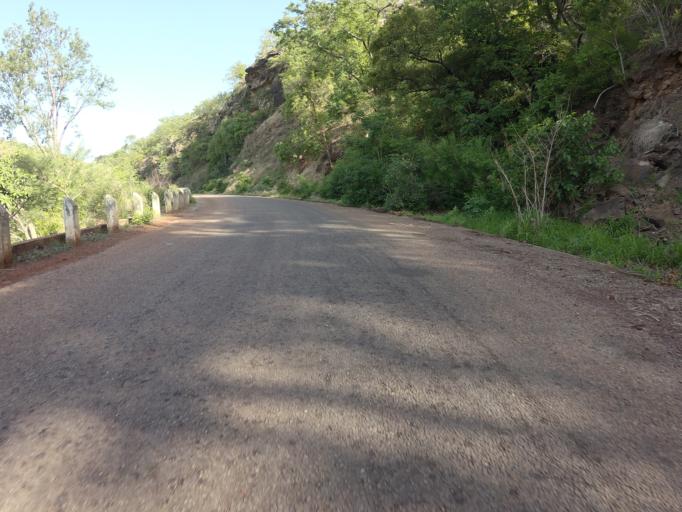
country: GH
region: Upper East
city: Bawku
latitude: 10.6433
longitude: -0.1963
